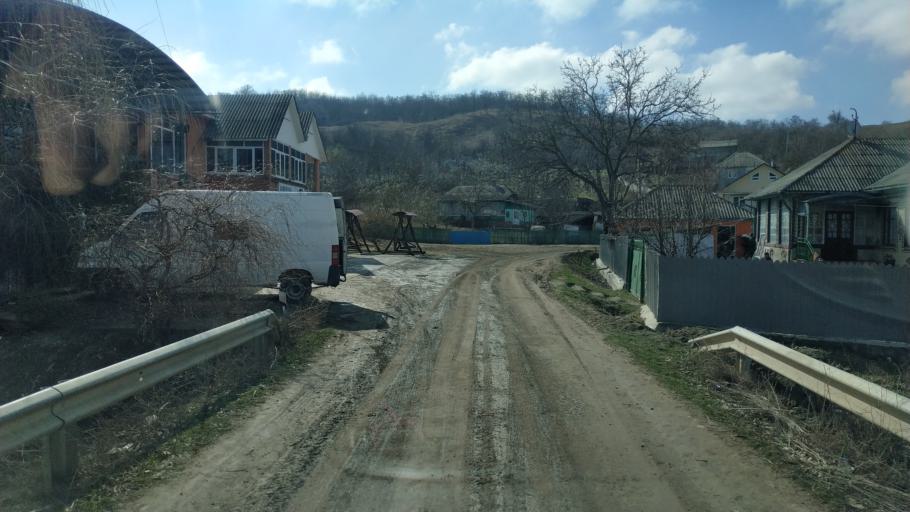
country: MD
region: Hincesti
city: Hincesti
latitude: 46.8821
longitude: 28.6200
